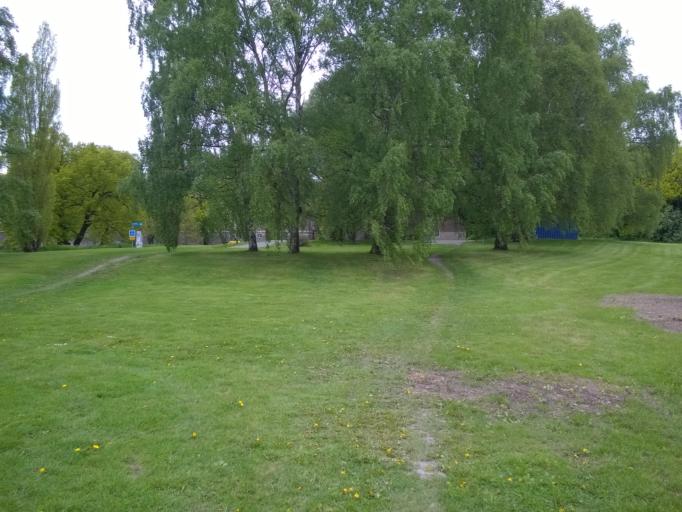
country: SE
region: Stockholm
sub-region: Norrtalje Kommun
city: Bergshamra
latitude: 59.3670
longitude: 18.0567
